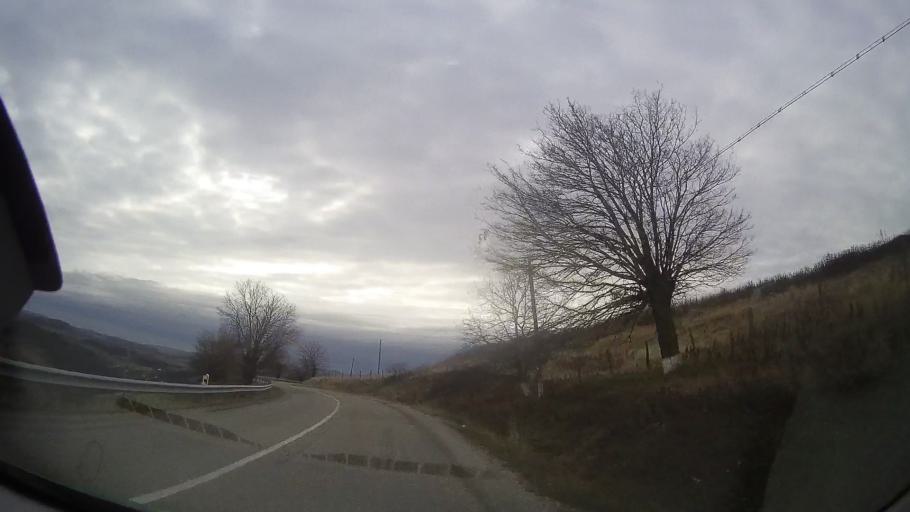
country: RO
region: Bistrita-Nasaud
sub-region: Comuna Budesti
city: Budesti
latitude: 46.8887
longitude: 24.2411
